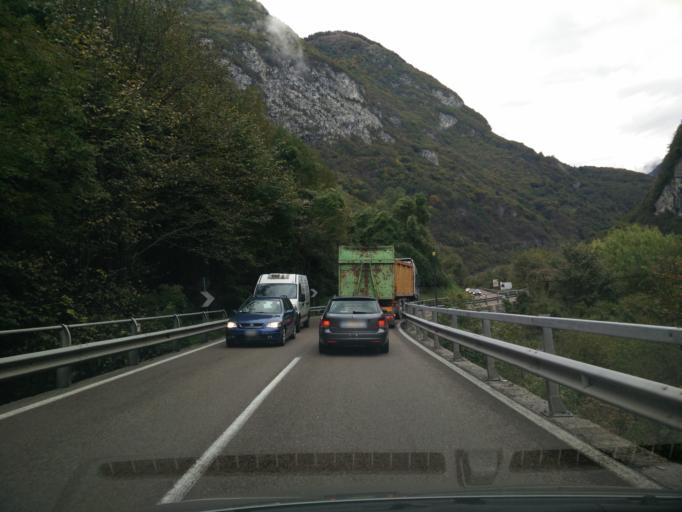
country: IT
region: Veneto
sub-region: Provincia di Belluno
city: Castello Lavazzo
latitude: 46.2897
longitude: 12.3103
